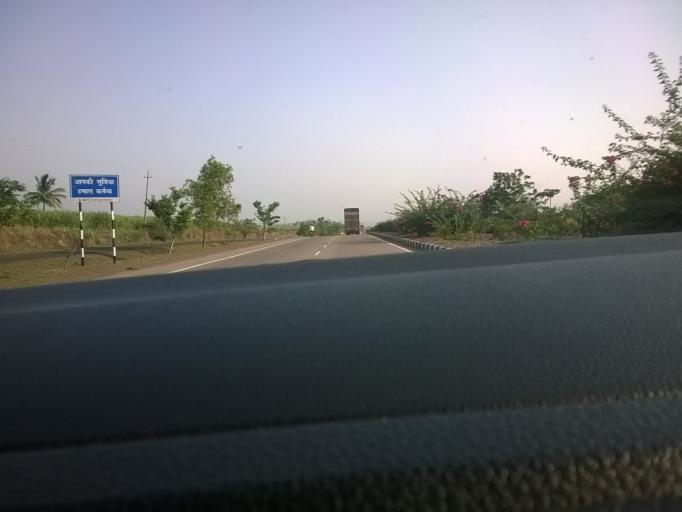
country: IN
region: Maharashtra
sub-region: Kolhapur
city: Kagal
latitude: 16.5335
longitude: 74.3199
